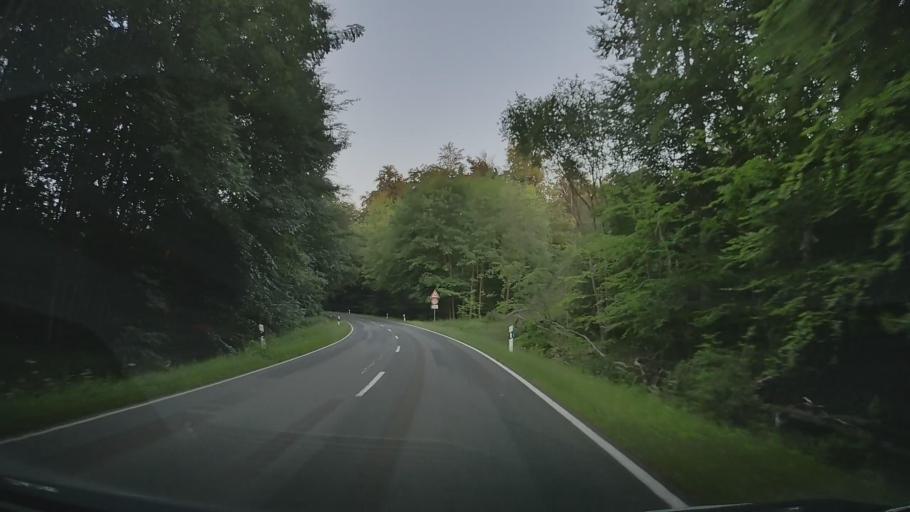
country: DE
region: Lower Saxony
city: Aerzen
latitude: 52.0265
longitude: 9.2799
